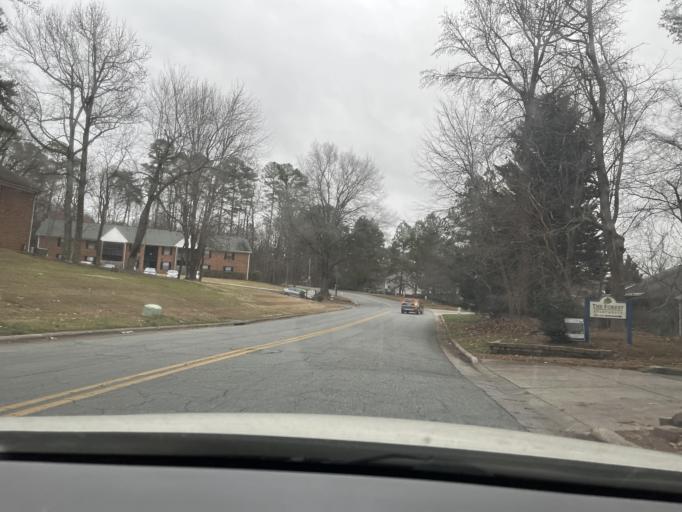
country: US
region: North Carolina
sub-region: Guilford County
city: Greensboro
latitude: 36.0224
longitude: -79.7825
